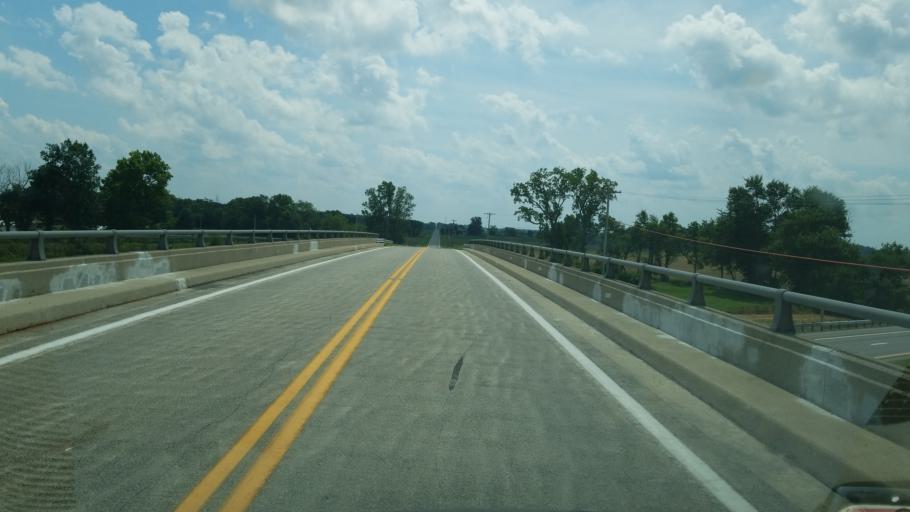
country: US
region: Ohio
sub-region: Hancock County
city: Findlay
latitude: 40.9779
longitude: -83.7275
